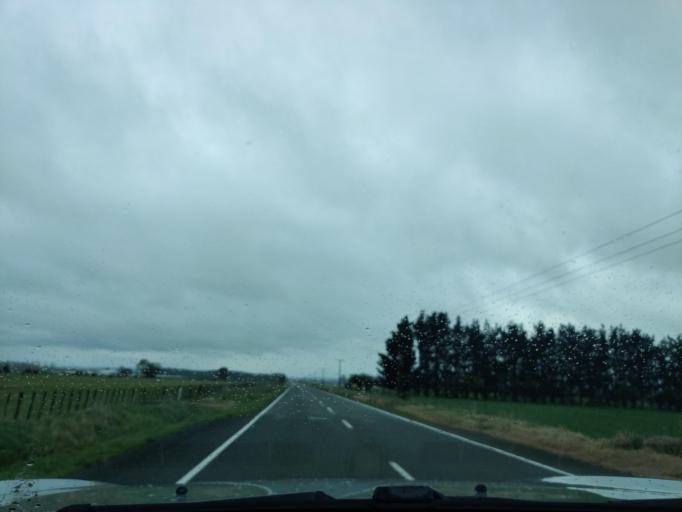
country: NZ
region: Hawke's Bay
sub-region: Hastings District
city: Hastings
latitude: -40.0130
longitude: 176.3676
